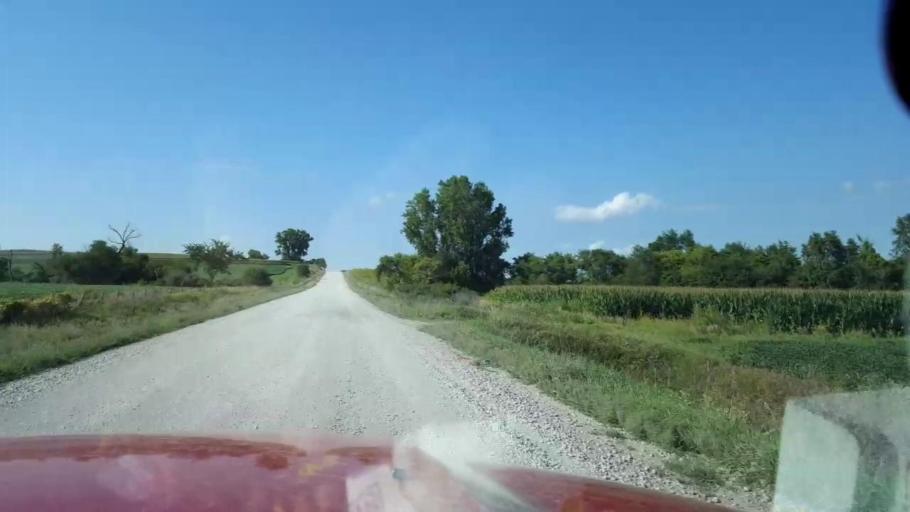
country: US
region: Iowa
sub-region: Pottawattamie County
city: Oakland
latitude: 41.2528
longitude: -95.5370
